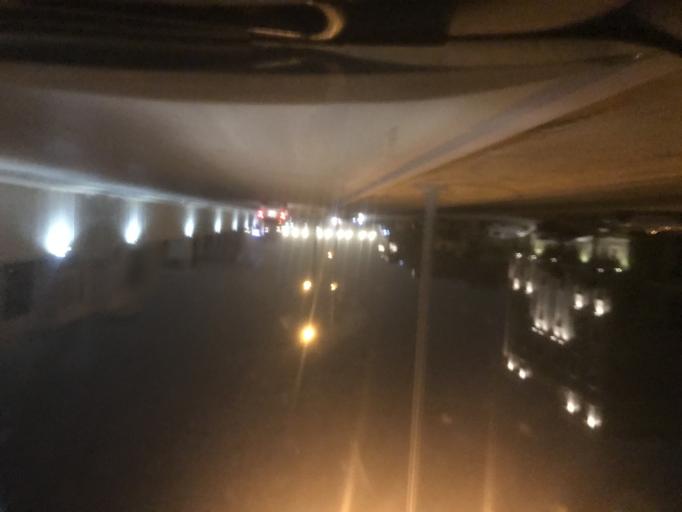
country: SA
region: Ar Riyad
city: Riyadh
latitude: 24.8308
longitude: 46.7341
